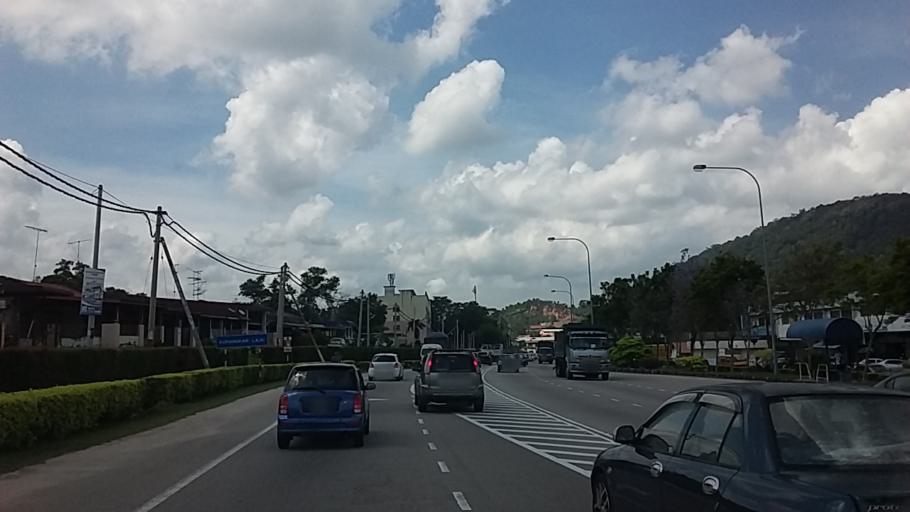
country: MY
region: Johor
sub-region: Daerah Batu Pahat
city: Batu Pahat
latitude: 1.8432
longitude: 102.9430
